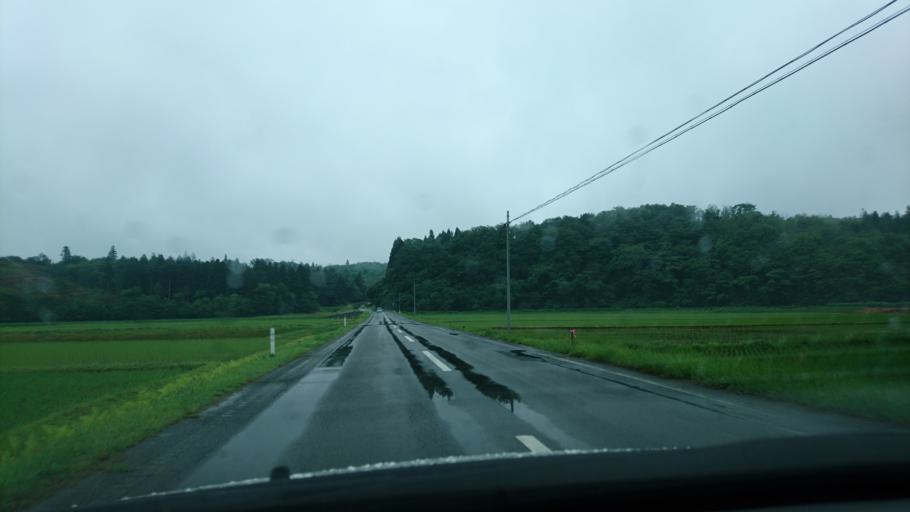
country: JP
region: Iwate
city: Ichinoseki
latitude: 38.9231
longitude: 141.0249
